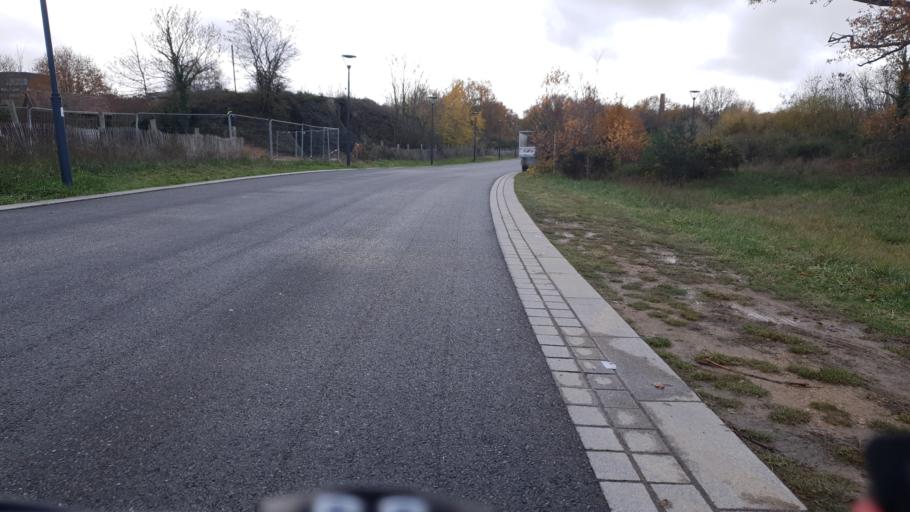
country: FR
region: Brittany
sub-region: Departement d'Ille-et-Vilaine
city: Rennes
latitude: 48.0976
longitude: -1.7042
